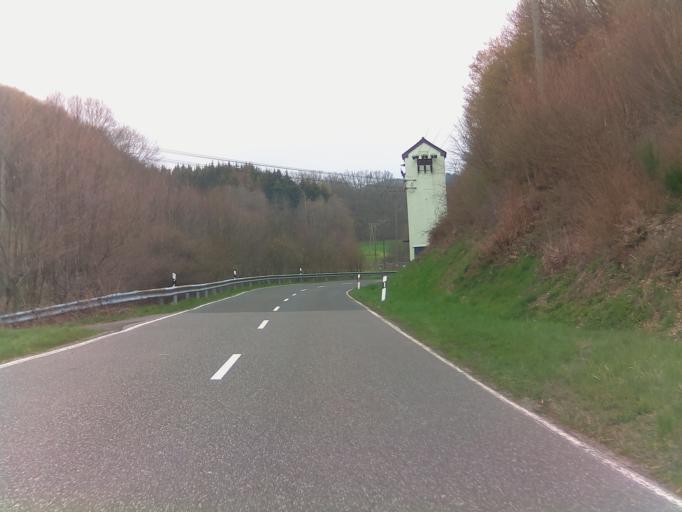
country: DE
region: Rheinland-Pfalz
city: Siesbach
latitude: 49.7327
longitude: 7.2375
